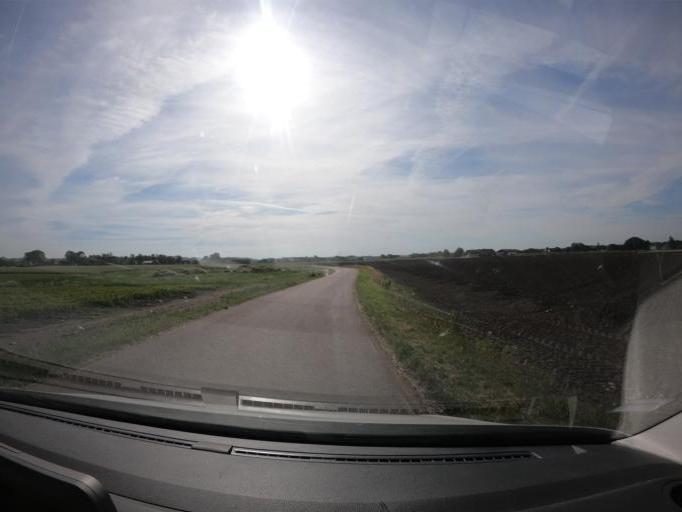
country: SE
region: Skane
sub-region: Angelholms Kommun
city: Vejbystrand
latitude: 56.3556
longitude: 12.7712
